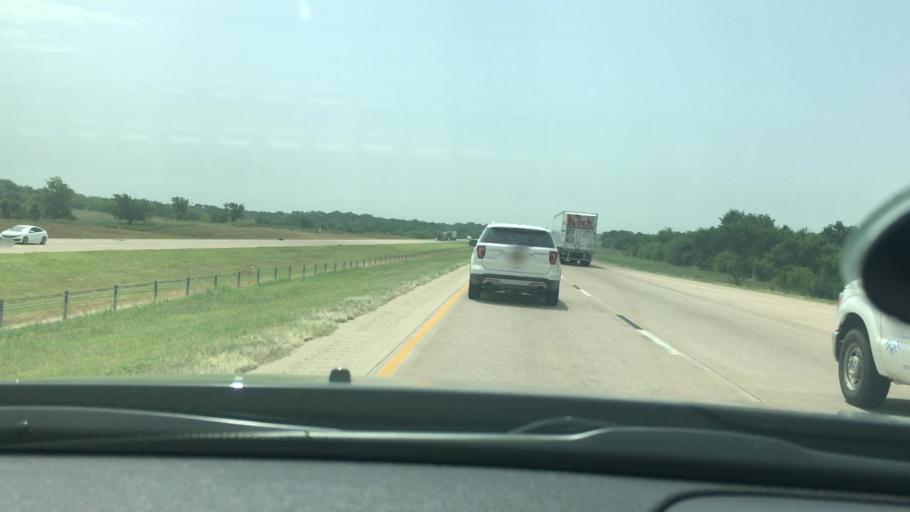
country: US
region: Oklahoma
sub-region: Garvin County
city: Pauls Valley
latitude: 34.7015
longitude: -97.2413
